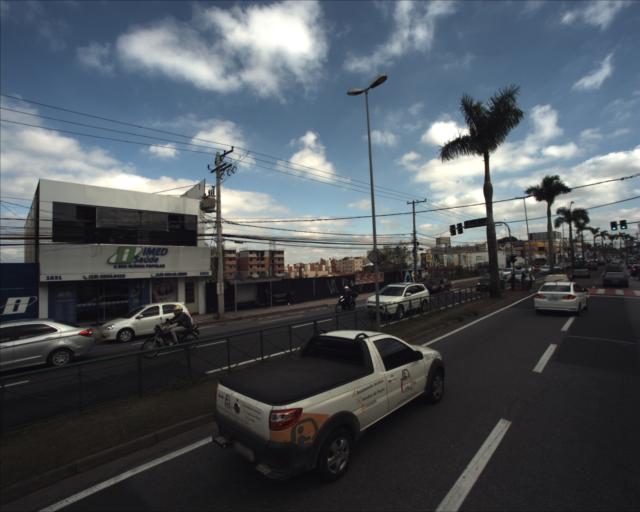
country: BR
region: Sao Paulo
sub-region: Sorocaba
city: Sorocaba
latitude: -23.5068
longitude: -47.4834
